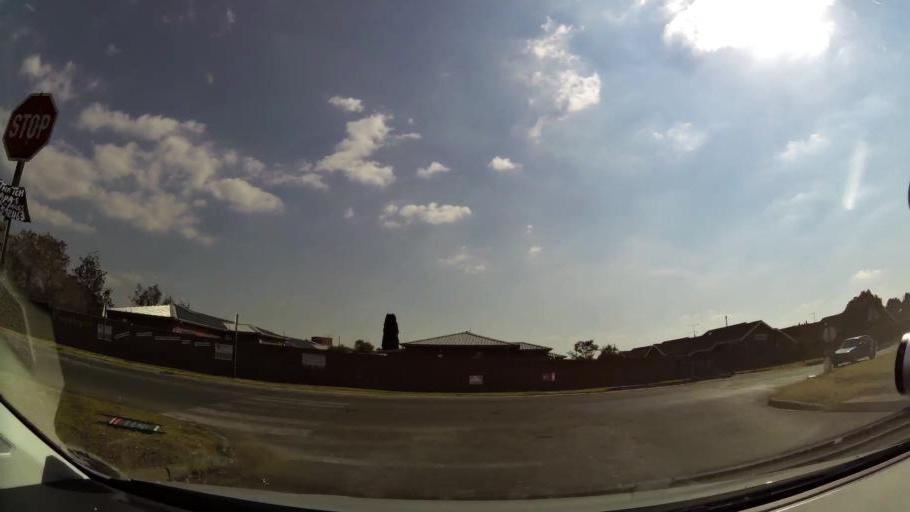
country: ZA
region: Gauteng
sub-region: City of Johannesburg Metropolitan Municipality
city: Modderfontein
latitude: -26.0799
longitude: 28.2344
